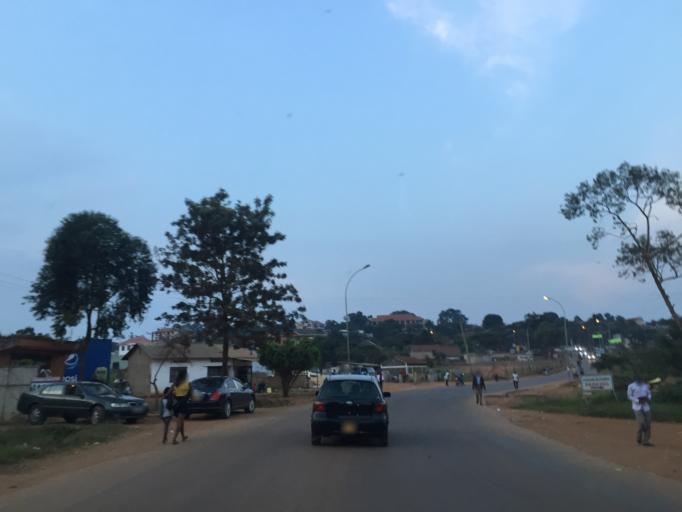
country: UG
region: Central Region
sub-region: Kampala District
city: Kampala
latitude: 0.2563
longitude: 32.6264
